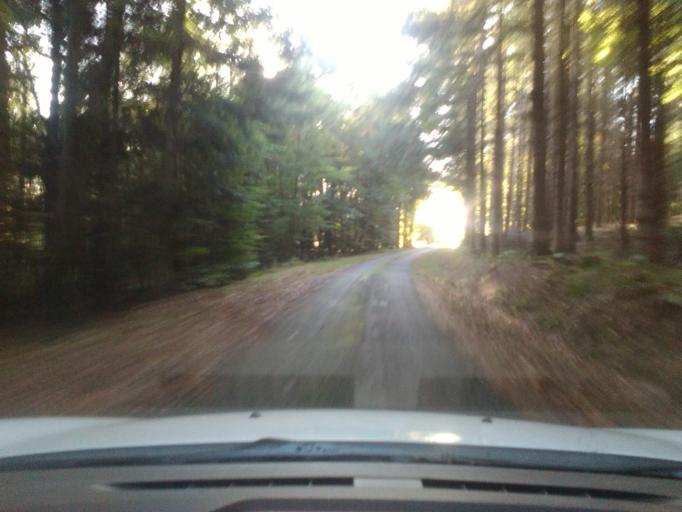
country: FR
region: Lorraine
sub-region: Departement des Vosges
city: Bruyeres
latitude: 48.2805
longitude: 6.7449
